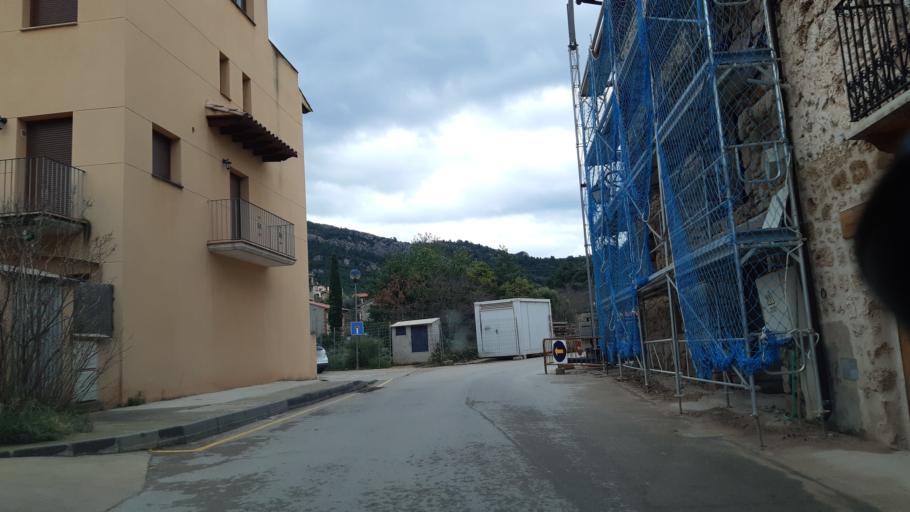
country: ES
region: Aragon
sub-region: Provincia de Teruel
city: Valderrobres
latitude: 40.8311
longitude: 0.1814
